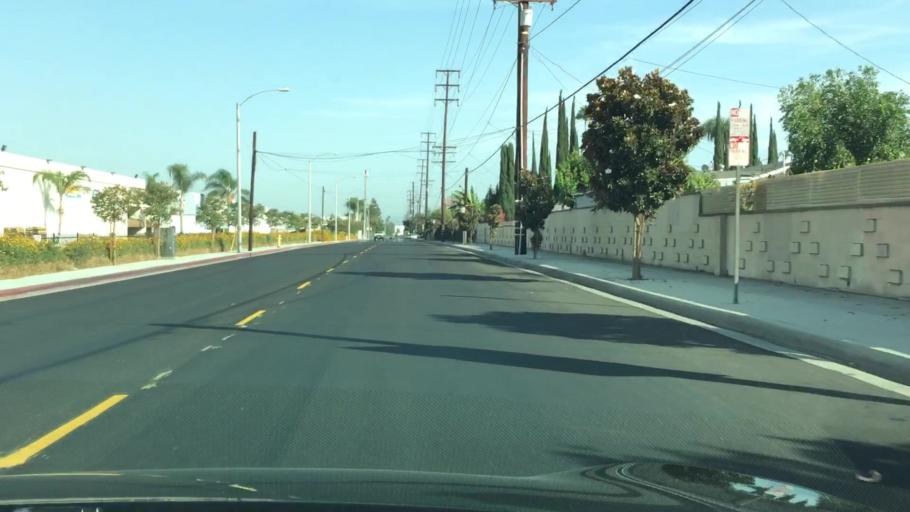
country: US
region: California
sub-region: Los Angeles County
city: Avocado Heights
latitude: 34.0228
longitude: -117.9845
